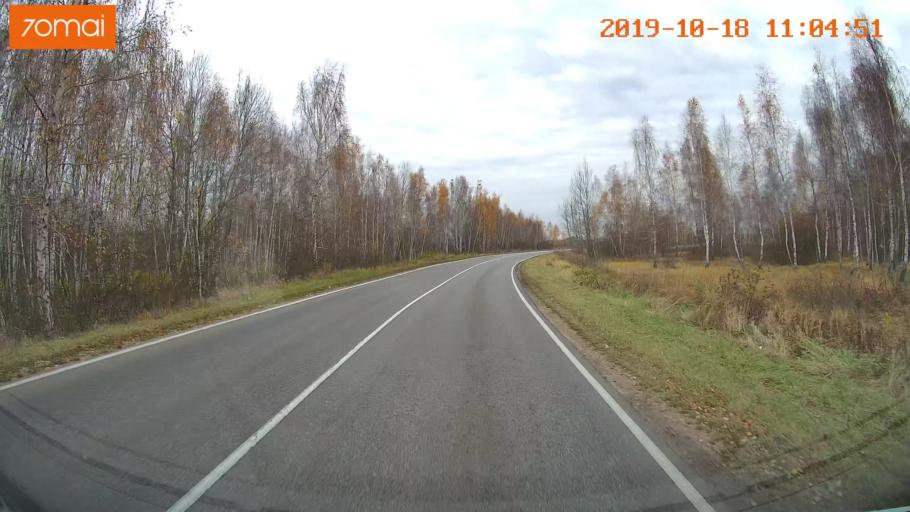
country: RU
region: Tula
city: Yepifan'
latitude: 53.8981
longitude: 38.5416
